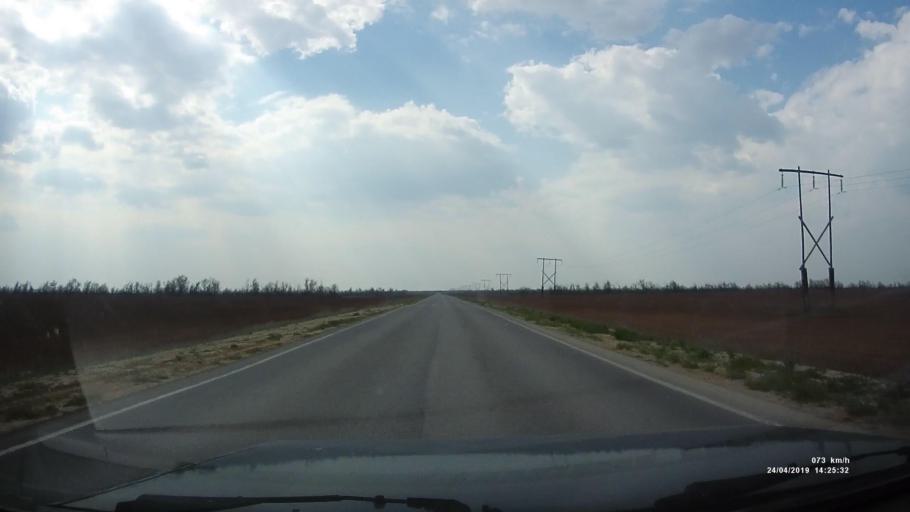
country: RU
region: Kalmykiya
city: Arshan'
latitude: 46.3312
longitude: 44.0803
